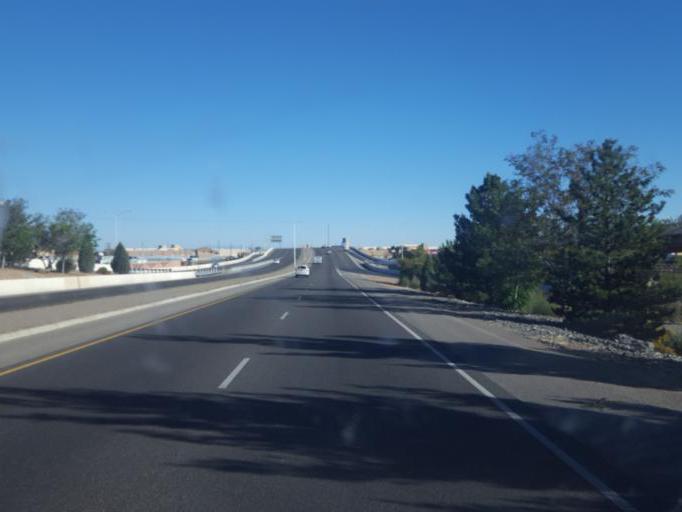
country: US
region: New Mexico
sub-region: Bernalillo County
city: Albuquerque
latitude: 35.1076
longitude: -106.7040
